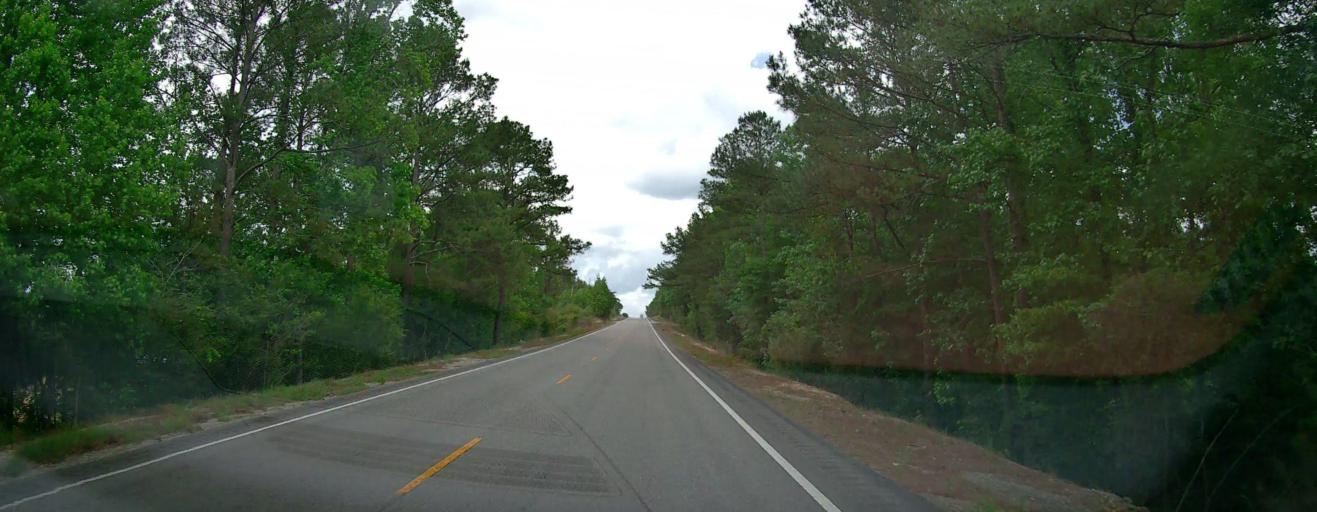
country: US
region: Alabama
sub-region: Marion County
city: Hamilton
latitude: 34.1296
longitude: -88.0281
